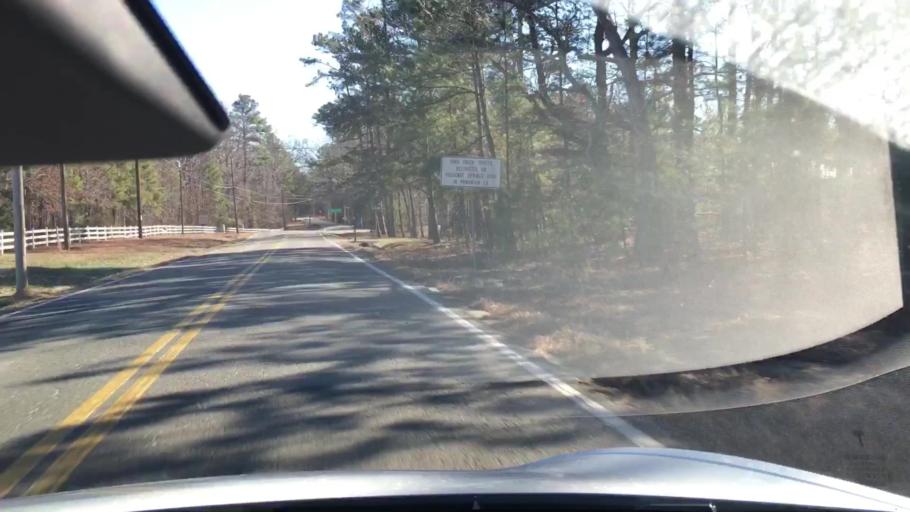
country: US
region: Virginia
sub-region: Henrico County
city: Short Pump
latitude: 37.5633
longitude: -77.7021
